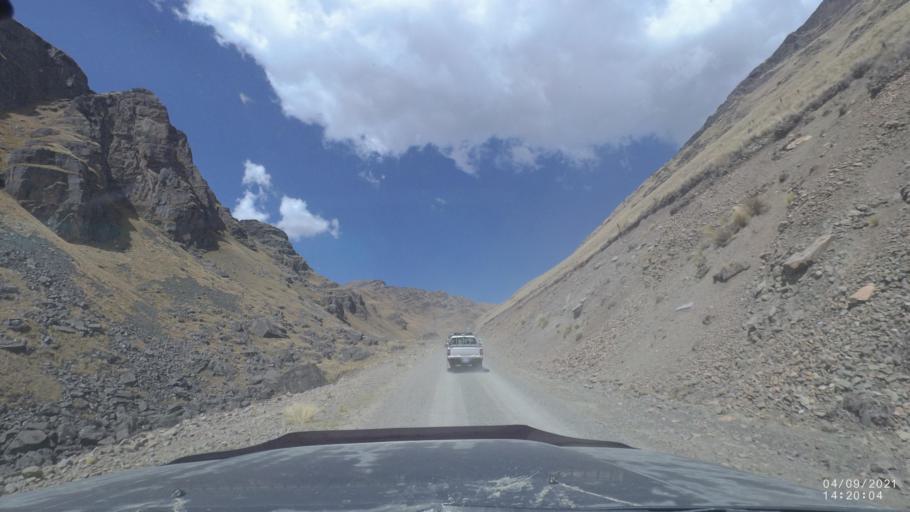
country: BO
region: Cochabamba
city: Sipe Sipe
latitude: -17.2344
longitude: -66.4218
